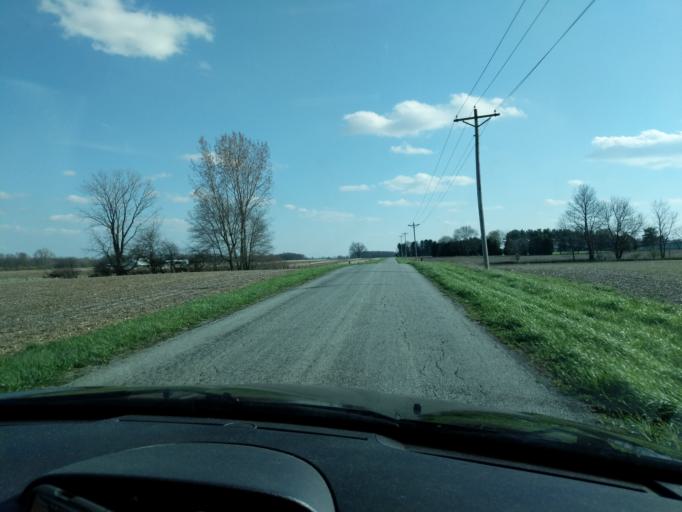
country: US
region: Ohio
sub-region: Champaign County
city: Urbana
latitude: 40.1459
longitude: -83.8151
